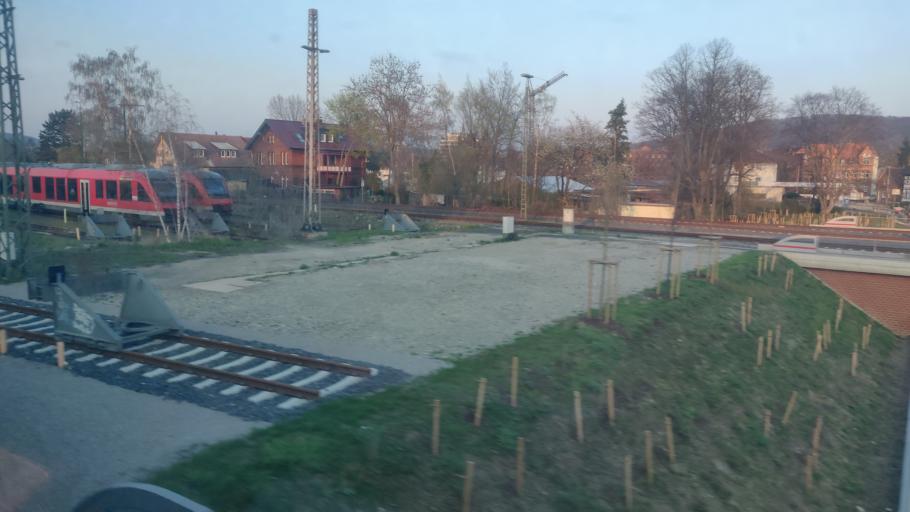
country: DE
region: Lower Saxony
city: Northeim
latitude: 51.7050
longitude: 9.9874
